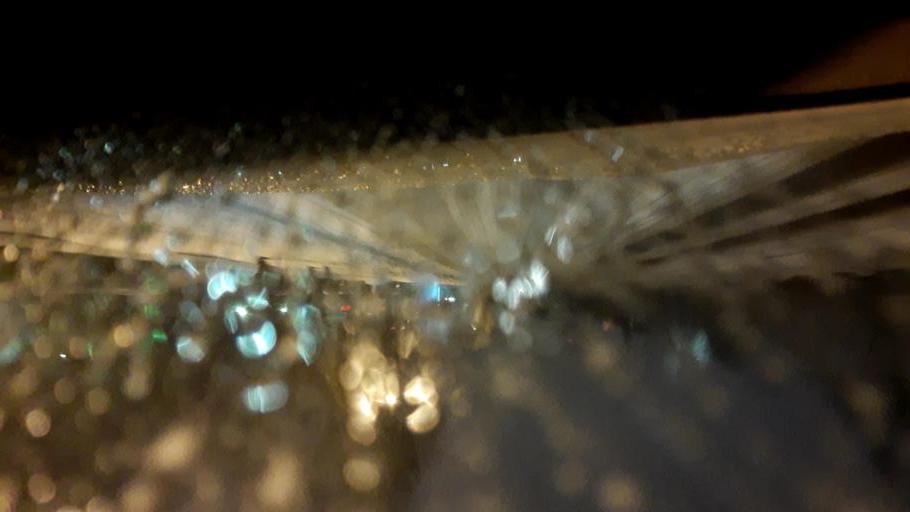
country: RU
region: Moscow
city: Khimki
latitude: 55.9029
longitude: 37.4393
